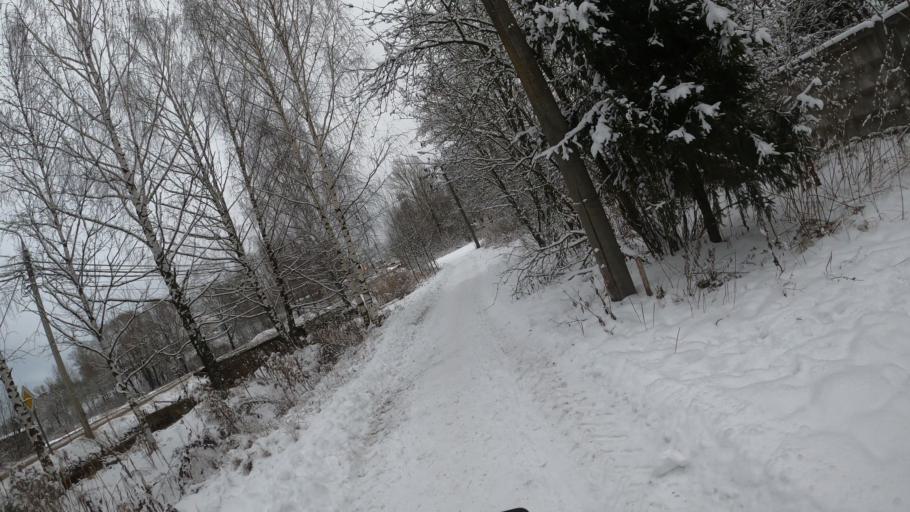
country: RU
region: Jaroslavl
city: Pereslavl'-Zalesskiy
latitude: 56.7395
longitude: 38.8939
